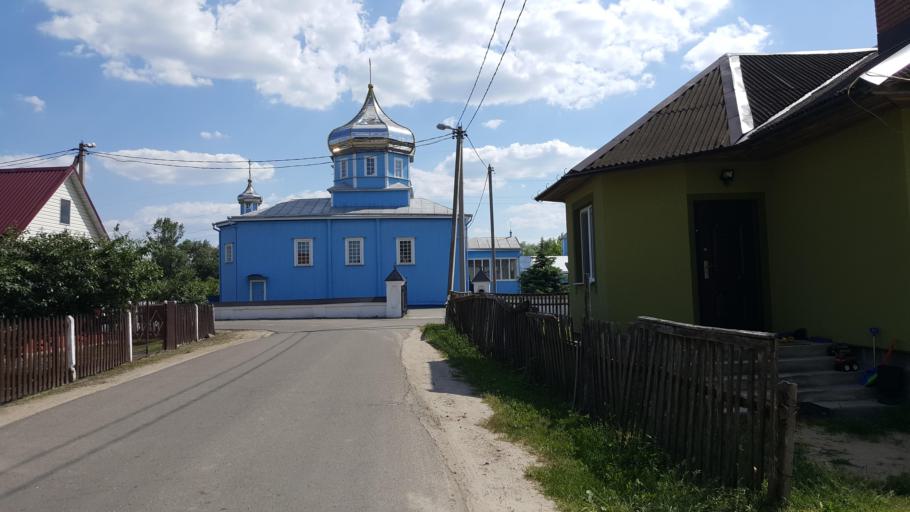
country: BY
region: Brest
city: Kobryn
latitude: 52.2173
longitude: 24.3606
